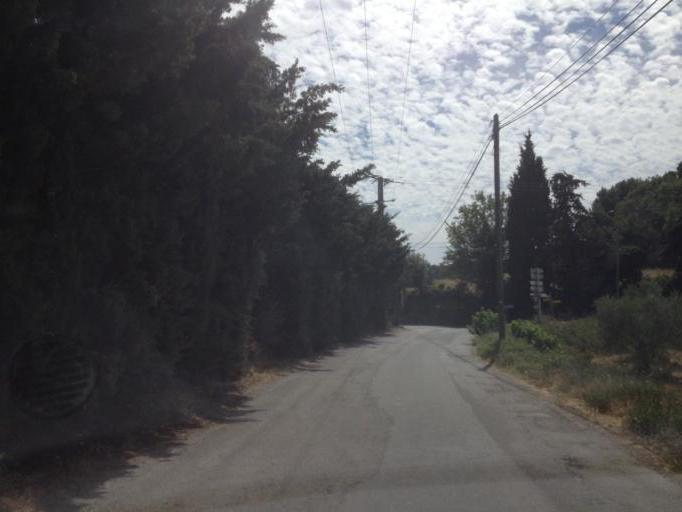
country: FR
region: Provence-Alpes-Cote d'Azur
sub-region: Departement du Vaucluse
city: Caromb
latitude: 44.1459
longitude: 5.0964
